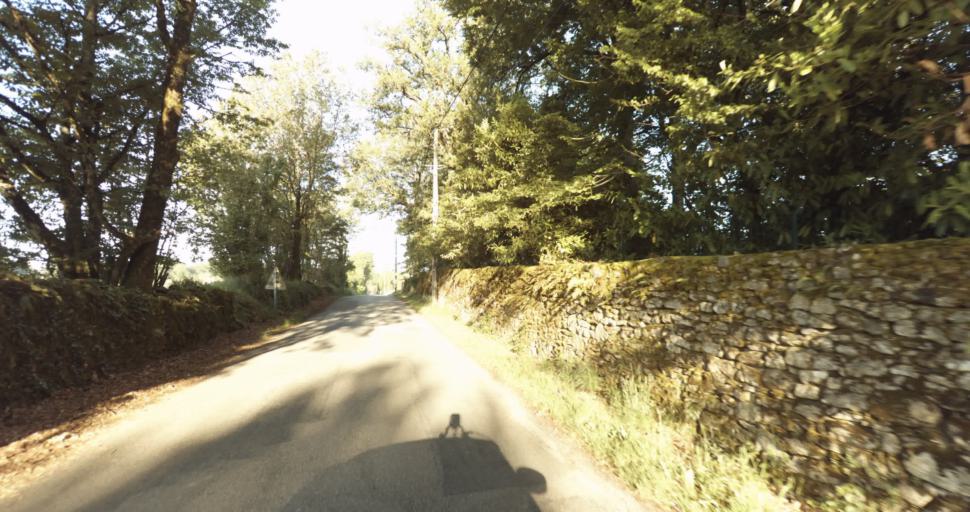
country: FR
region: Limousin
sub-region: Departement de la Haute-Vienne
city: Condat-sur-Vienne
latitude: 45.7810
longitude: 1.3013
